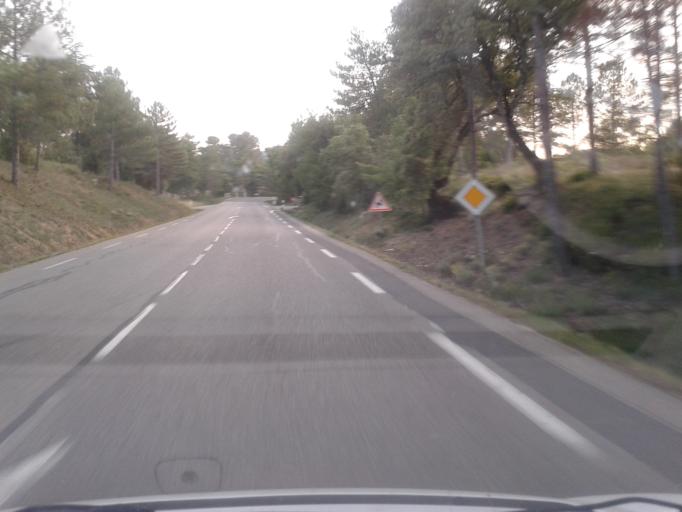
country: FR
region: Provence-Alpes-Cote d'Azur
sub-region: Departement du Var
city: Vinon-sur-Verdon
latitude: 43.7028
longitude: 5.7498
